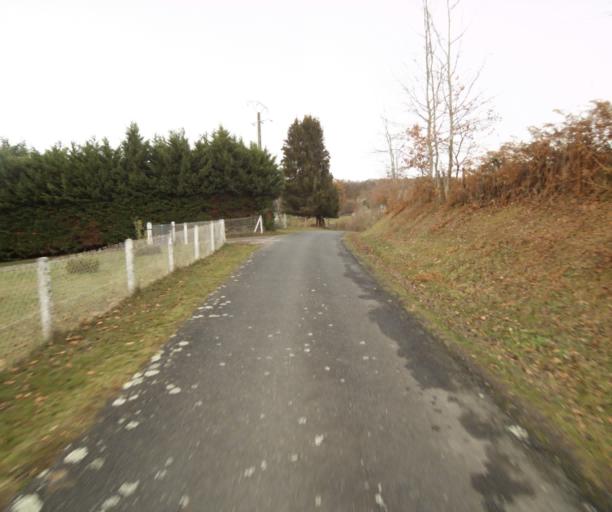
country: FR
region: Limousin
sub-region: Departement de la Correze
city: Saint-Mexant
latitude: 45.2549
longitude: 1.6558
